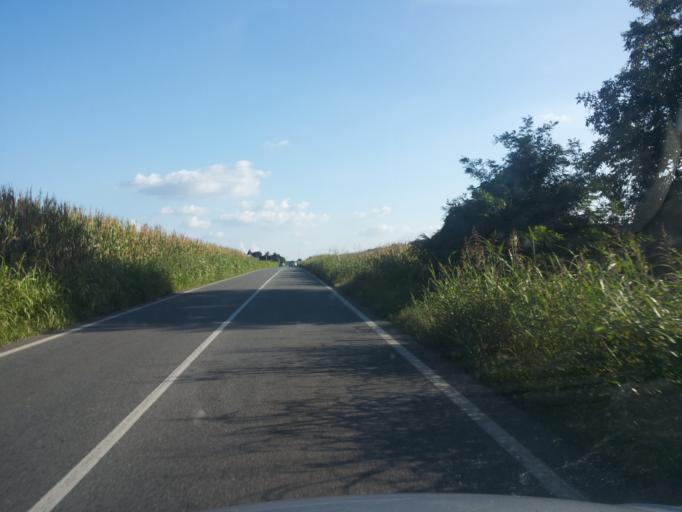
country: IT
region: Piedmont
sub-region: Provincia di Torino
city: Romano Canavese
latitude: 45.4012
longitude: 7.8835
